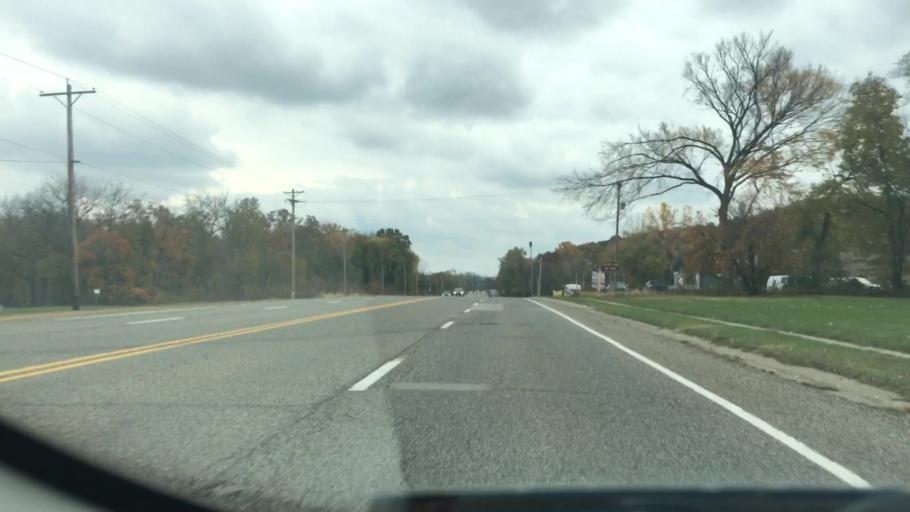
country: US
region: Illinois
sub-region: Peoria County
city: Peoria Heights
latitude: 40.7539
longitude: -89.5621
